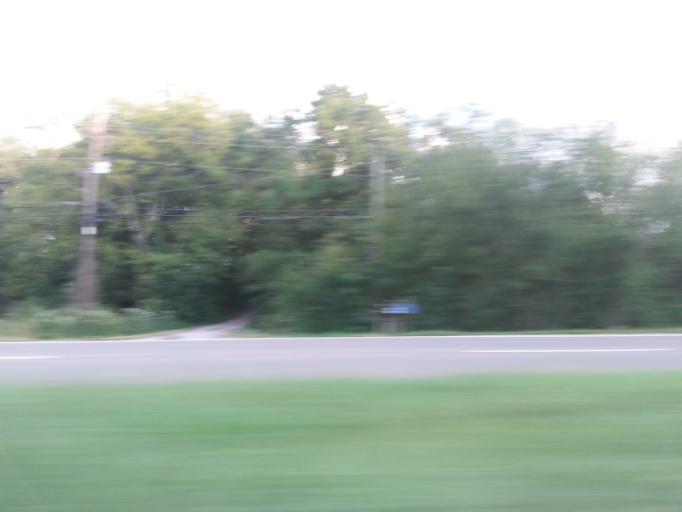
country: US
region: Tennessee
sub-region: Knox County
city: Mascot
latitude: 36.0560
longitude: -83.6975
